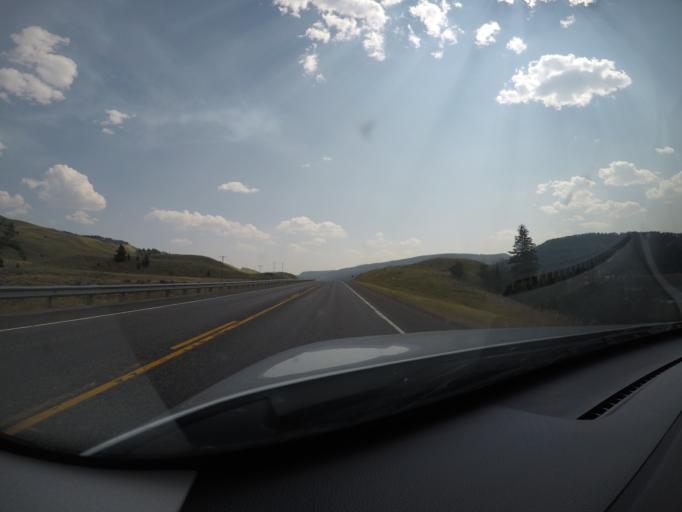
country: US
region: Montana
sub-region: Gallatin County
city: Big Sky
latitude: 44.9325
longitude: -111.6052
